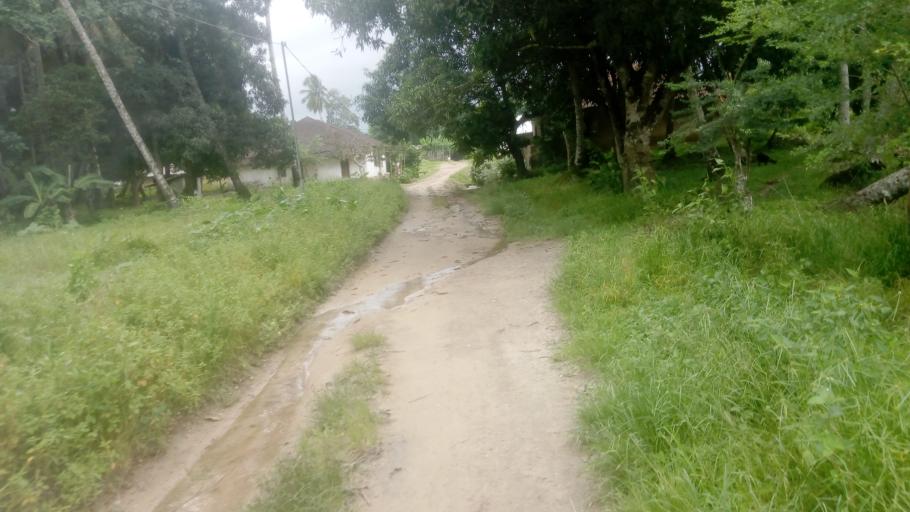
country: SL
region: Northern Province
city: Lunsar
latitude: 8.6791
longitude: -12.5363
